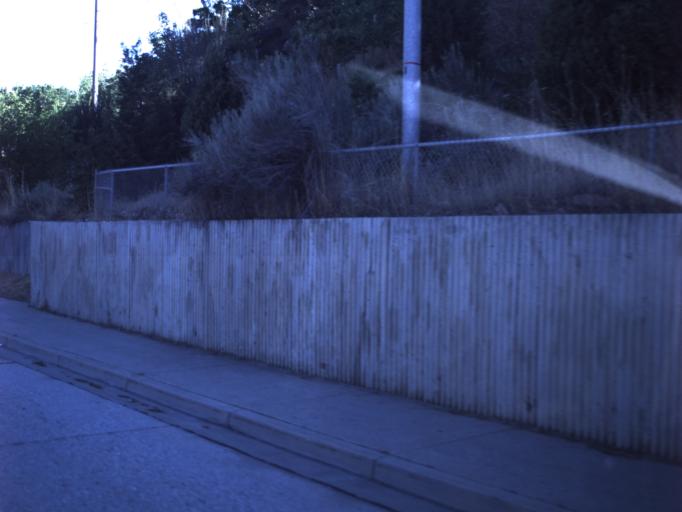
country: US
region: Utah
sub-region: Utah County
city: Provo
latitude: 40.2619
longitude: -111.6777
